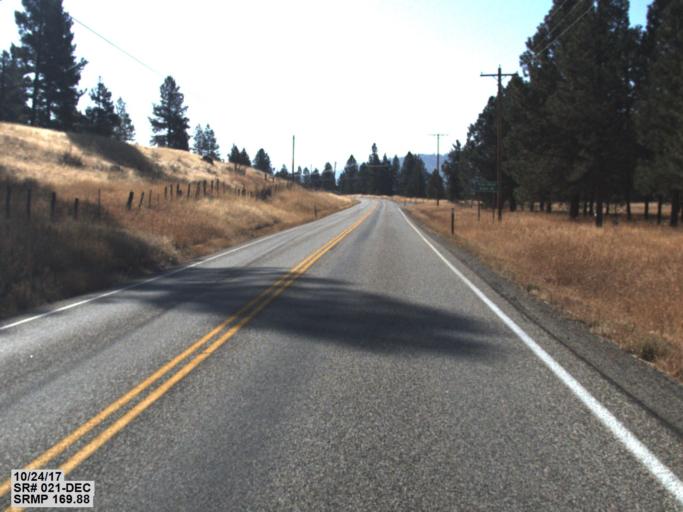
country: US
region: Washington
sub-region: Ferry County
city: Republic
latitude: 48.7416
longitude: -118.6601
